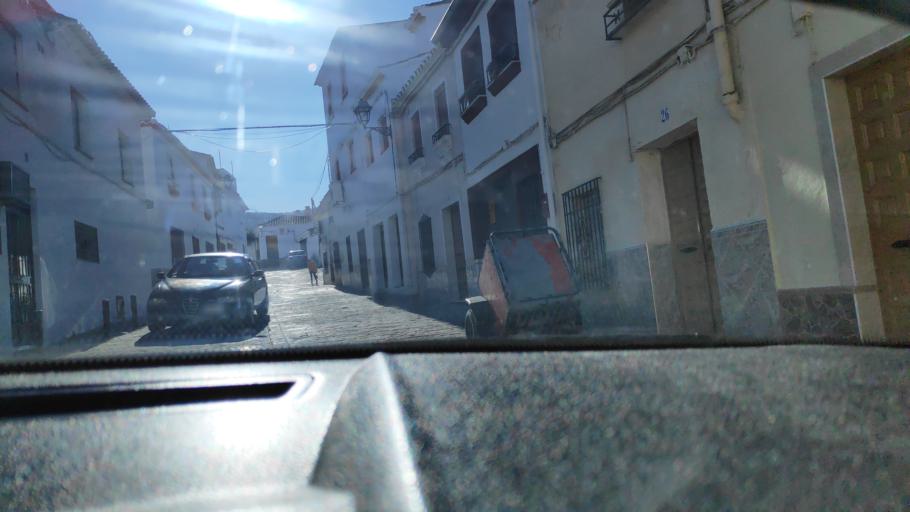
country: ES
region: Andalusia
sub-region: Province of Cordoba
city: Baena
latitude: 37.6132
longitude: -4.3337
